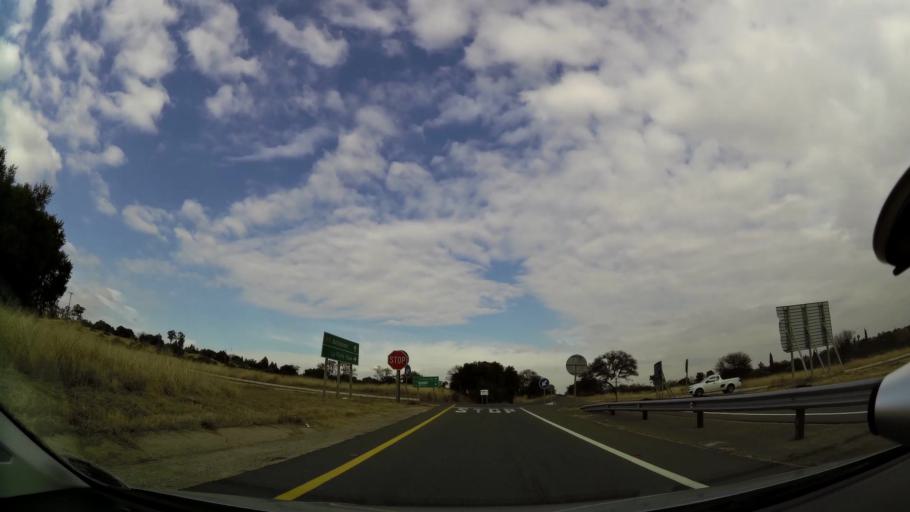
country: ZA
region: Orange Free State
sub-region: Fezile Dabi District Municipality
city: Kroonstad
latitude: -27.6878
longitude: 27.2429
